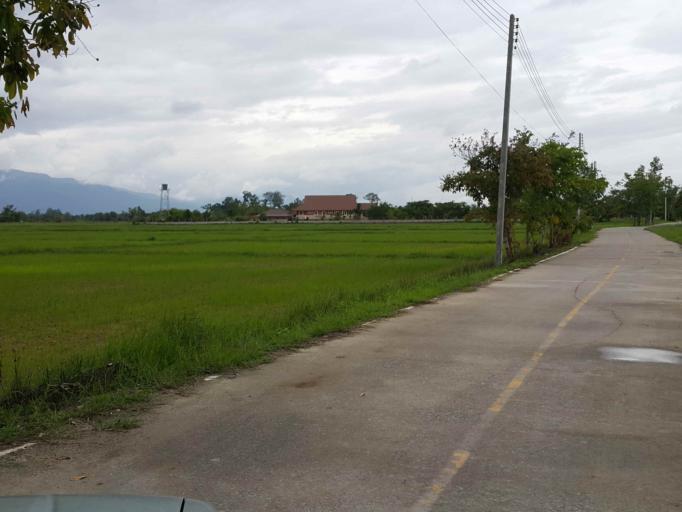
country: TH
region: Chiang Mai
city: San Sai
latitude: 18.8205
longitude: 99.0739
